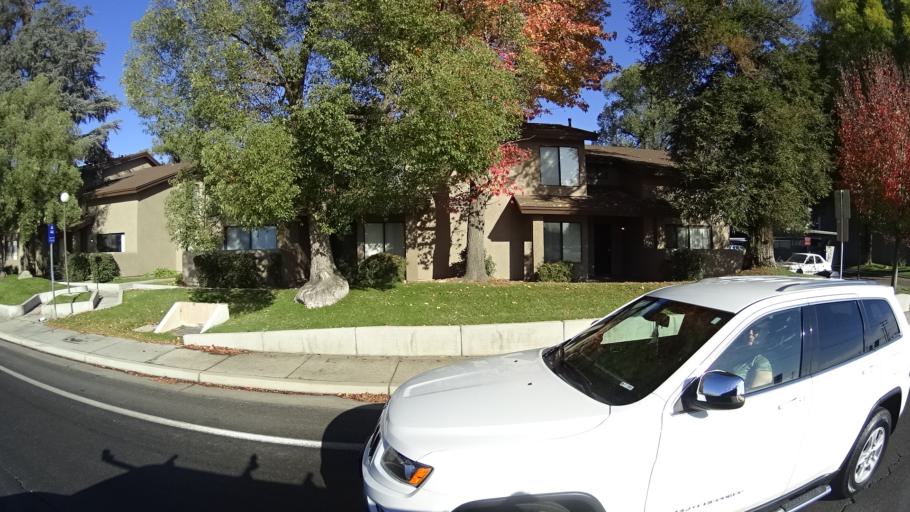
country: US
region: California
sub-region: Kern County
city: Greenacres
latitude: 35.3183
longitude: -119.0755
